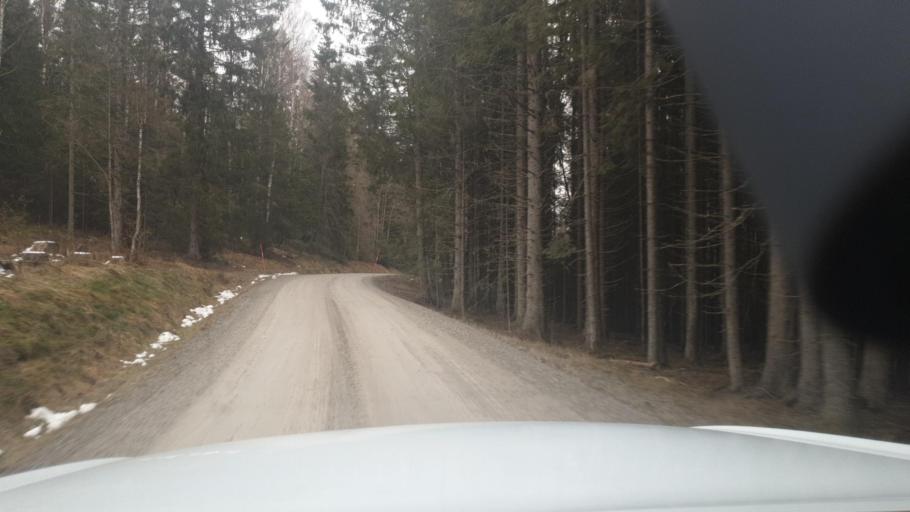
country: SE
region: Vaermland
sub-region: Sunne Kommun
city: Sunne
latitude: 59.8546
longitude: 12.9333
